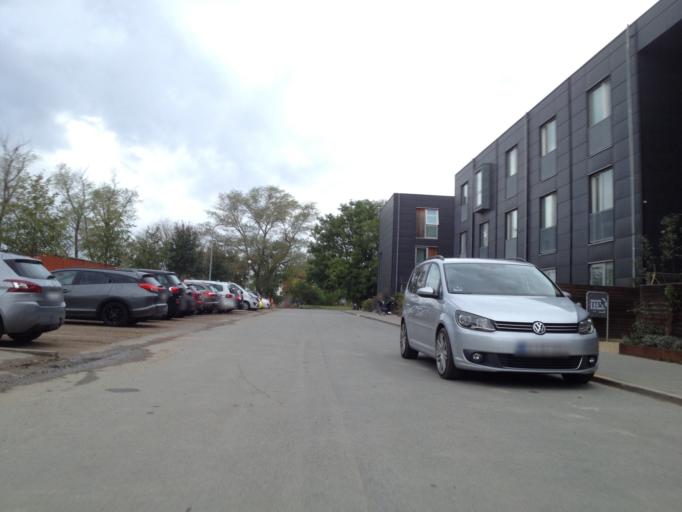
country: DK
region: Capital Region
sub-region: Kobenhavn
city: Christianshavn
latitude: 55.6858
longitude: 12.6141
